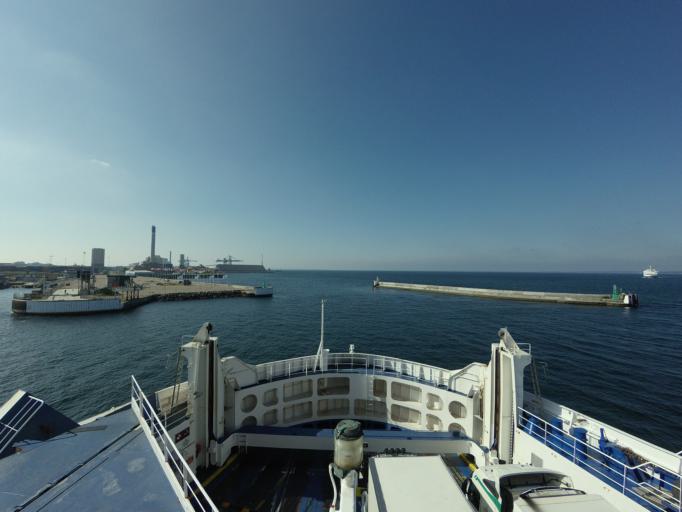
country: SE
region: Skane
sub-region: Helsingborg
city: Helsingborg
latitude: 56.0414
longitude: 12.6875
